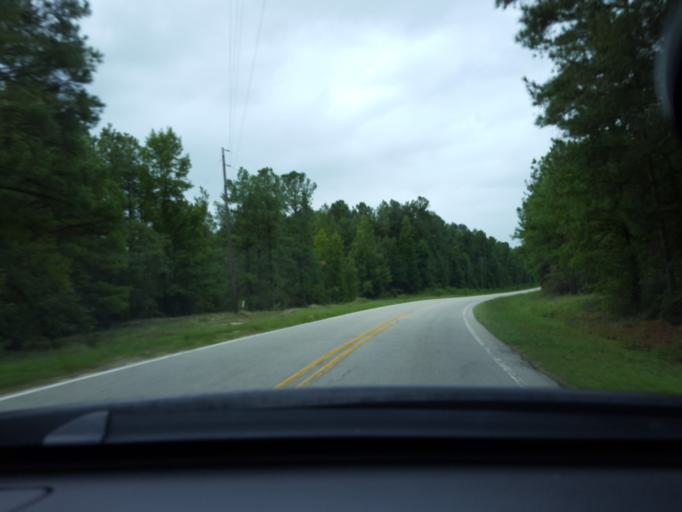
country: US
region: North Carolina
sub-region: Sampson County
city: Clinton
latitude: 34.7856
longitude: -78.3225
